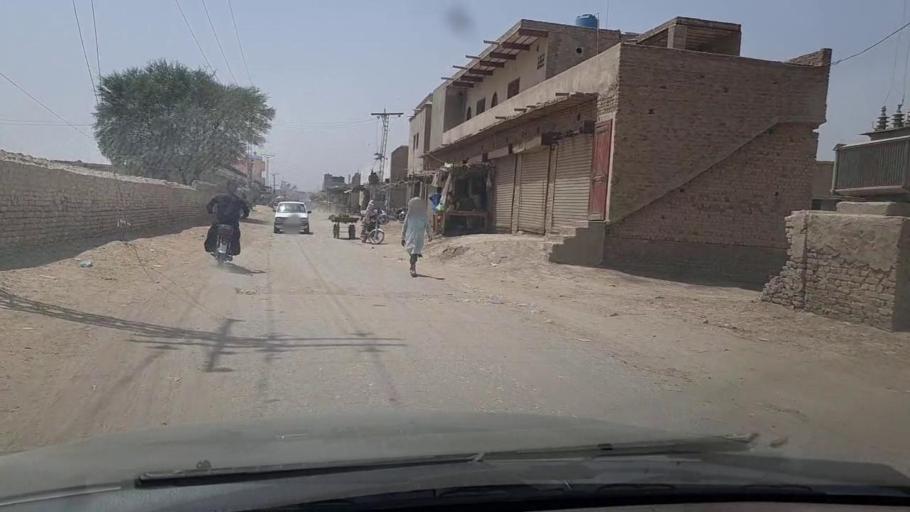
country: PK
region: Sindh
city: Miro Khan
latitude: 27.7610
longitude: 68.1003
